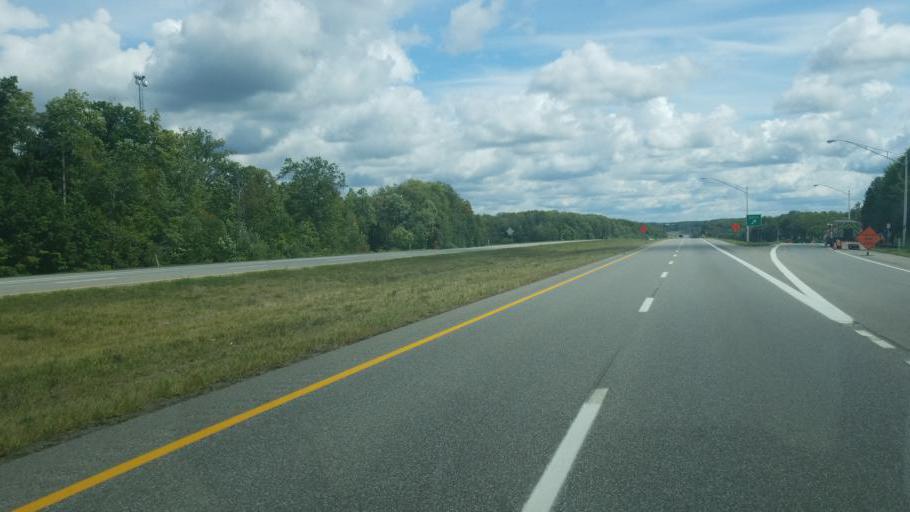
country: US
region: Ohio
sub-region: Portage County
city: Mantua
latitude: 41.3839
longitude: -81.2221
